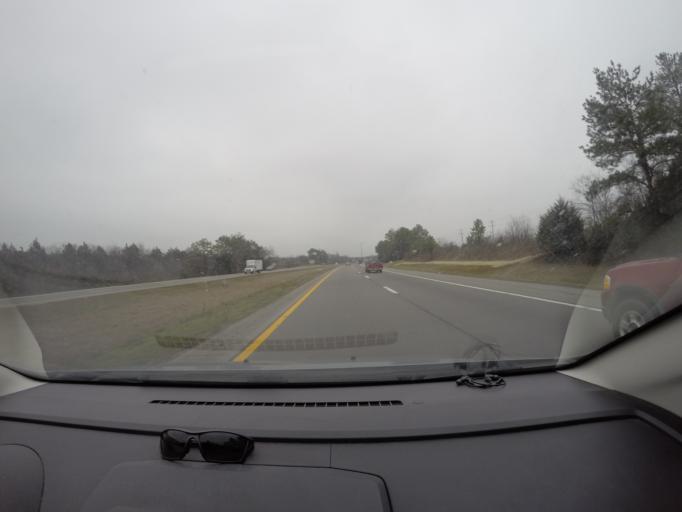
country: US
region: Tennessee
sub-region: Rutherford County
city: Murfreesboro
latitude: 35.7983
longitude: -86.3816
